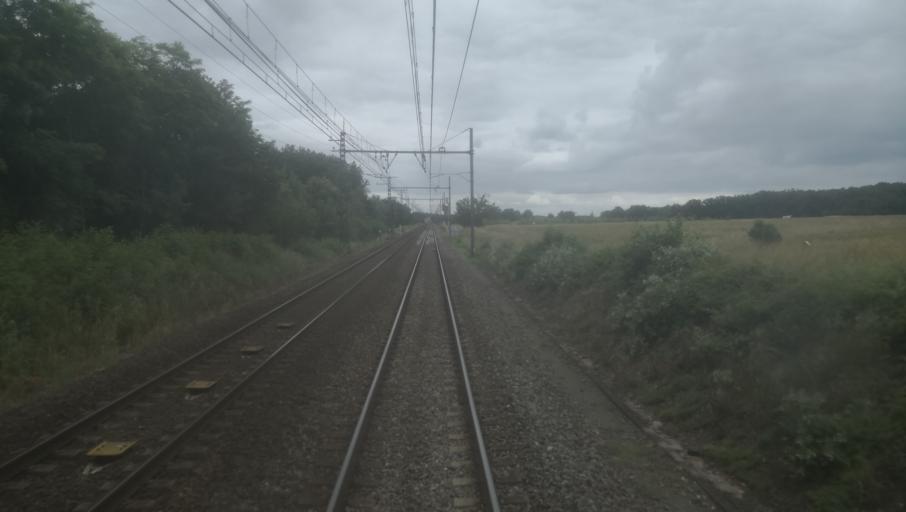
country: FR
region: Midi-Pyrenees
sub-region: Departement du Tarn-et-Garonne
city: Finhan
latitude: 43.9051
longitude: 1.2644
